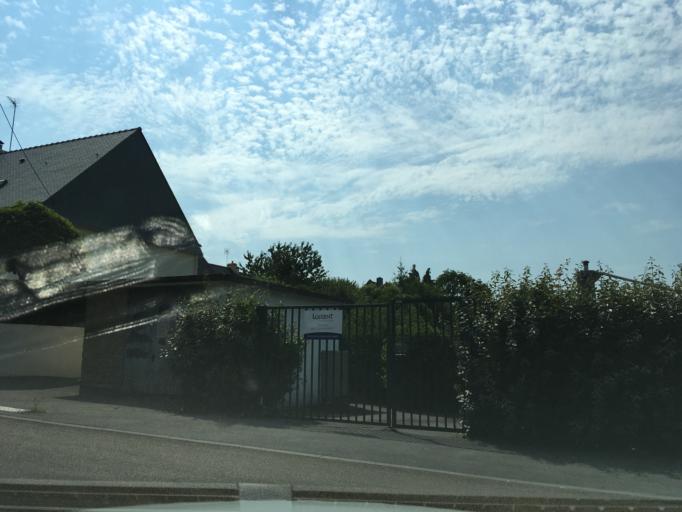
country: FR
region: Brittany
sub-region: Departement du Morbihan
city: Lorient
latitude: 47.7699
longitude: -3.3839
